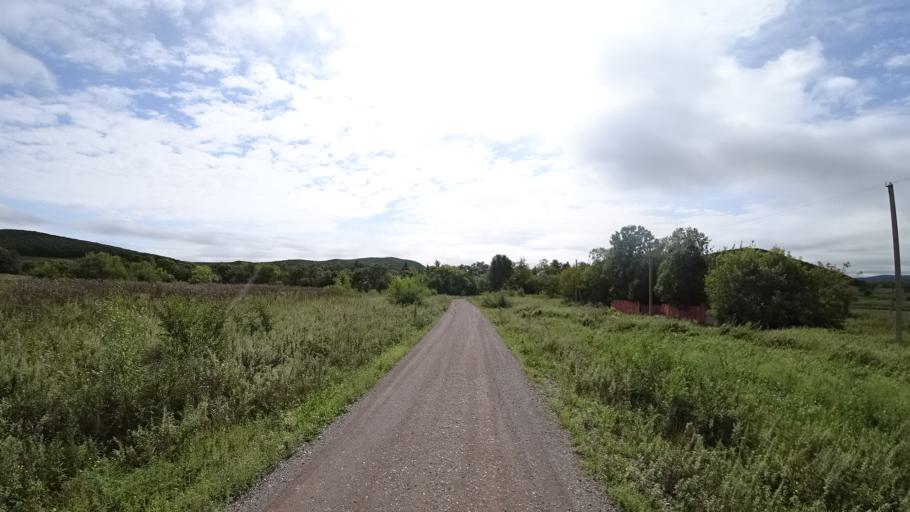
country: RU
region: Primorskiy
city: Lyalichi
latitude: 44.1399
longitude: 132.3754
